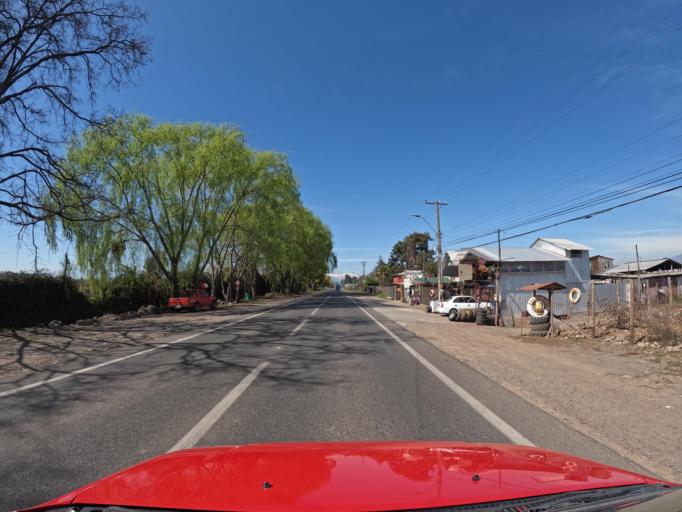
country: CL
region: Maule
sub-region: Provincia de Curico
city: Teno
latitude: -34.9622
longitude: -71.0833
